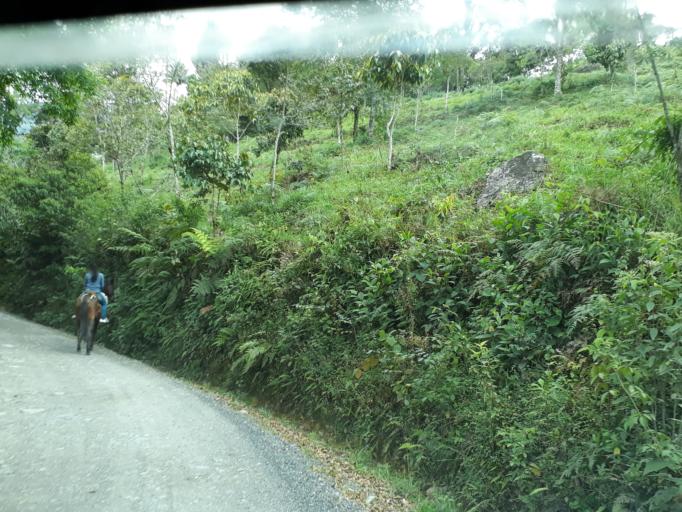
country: CO
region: Cundinamarca
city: Topaipi
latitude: 5.2790
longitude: -74.1958
